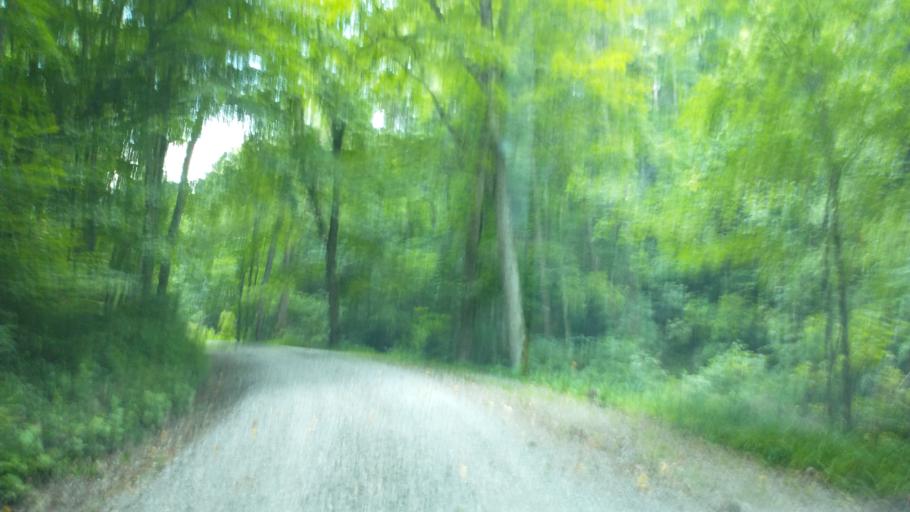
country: US
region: West Virginia
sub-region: Mercer County
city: Athens
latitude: 37.4287
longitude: -80.9971
